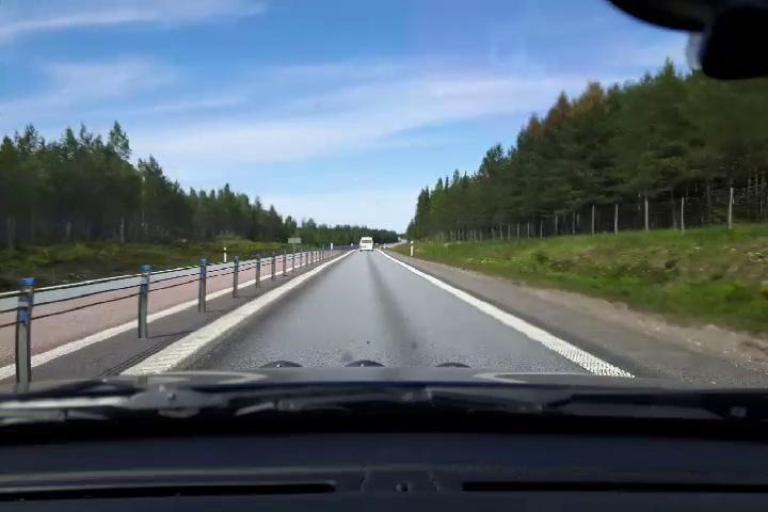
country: SE
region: Gaevleborg
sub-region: Gavle Kommun
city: Gavle
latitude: 60.8074
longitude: 17.0820
